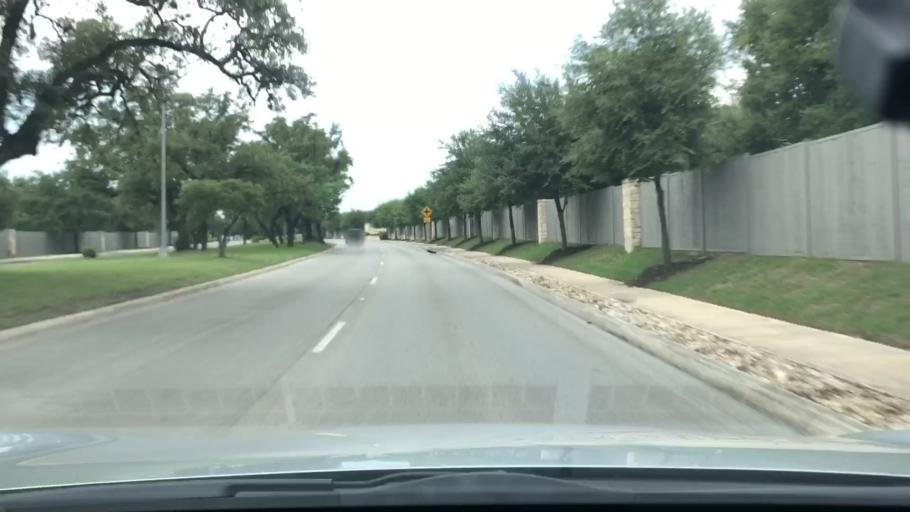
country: US
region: Texas
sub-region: Bexar County
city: Leon Valley
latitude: 29.4551
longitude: -98.6687
